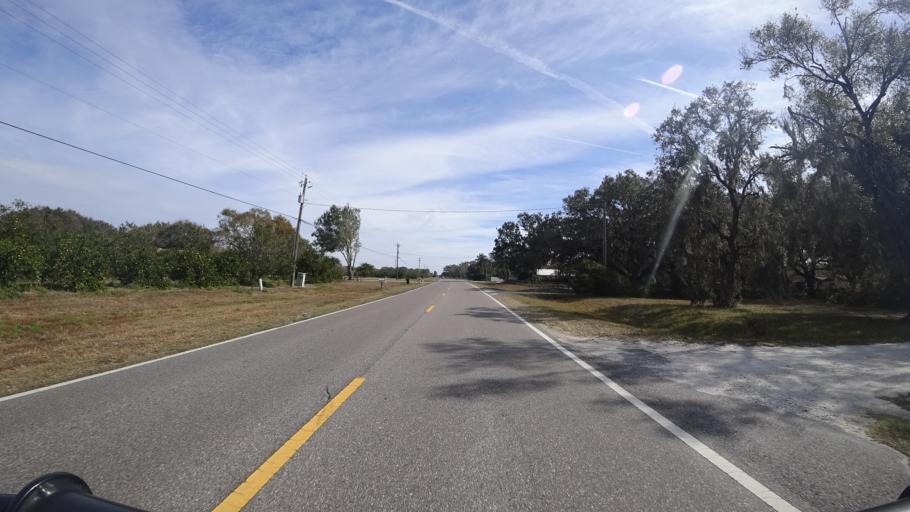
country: US
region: Florida
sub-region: Manatee County
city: Ellenton
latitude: 27.5757
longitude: -82.4169
